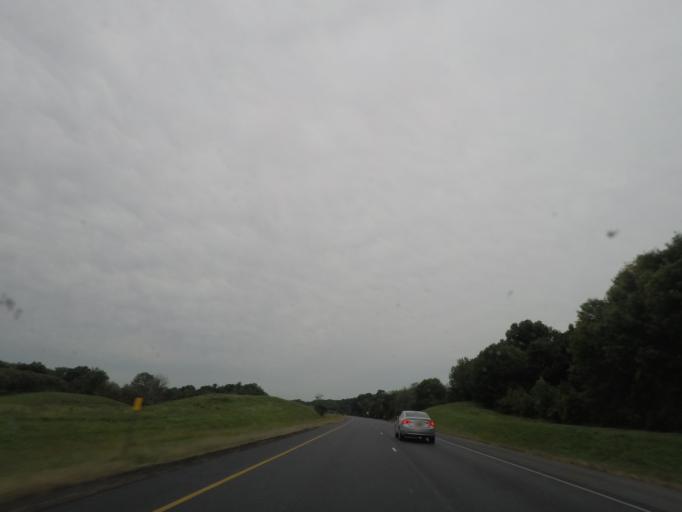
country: US
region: New York
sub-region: Rensselaer County
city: Nassau
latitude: 42.4837
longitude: -73.6367
